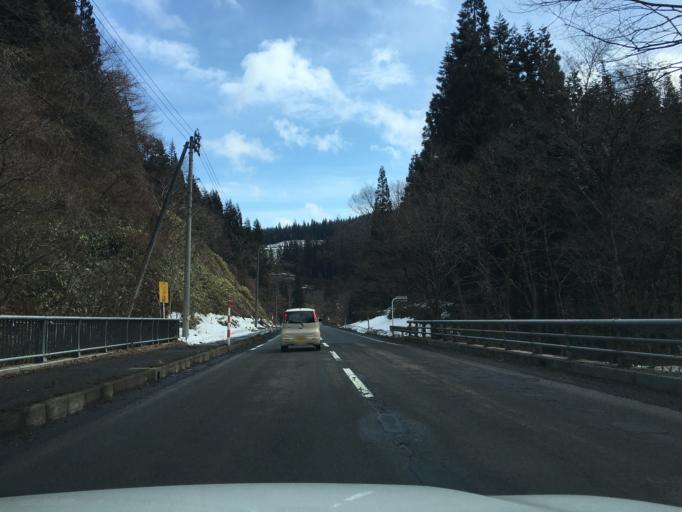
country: JP
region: Akita
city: Takanosu
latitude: 39.9990
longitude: 140.2693
